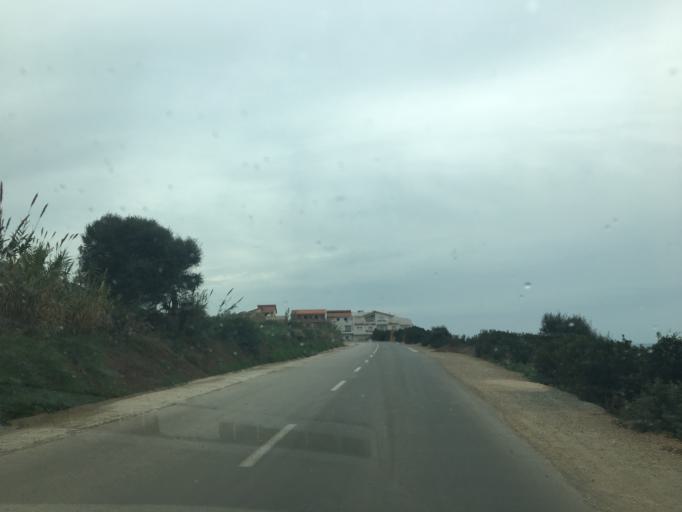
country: DZ
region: Tipaza
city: Tipasa
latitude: 36.6403
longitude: 2.3728
